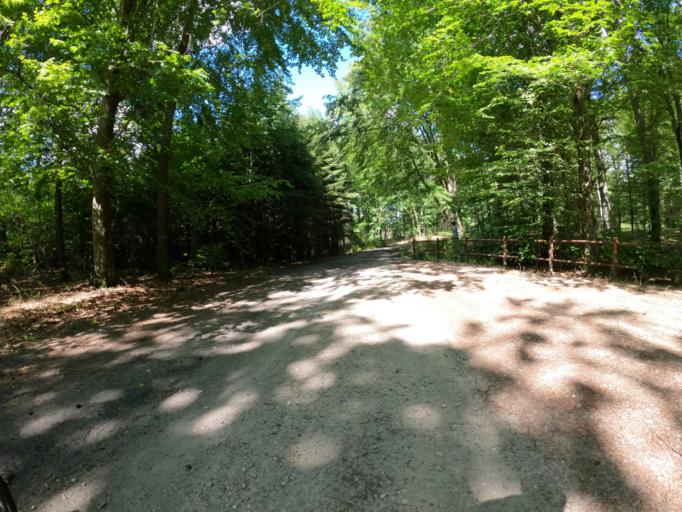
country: PL
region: West Pomeranian Voivodeship
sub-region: Powiat swidwinski
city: Swidwin
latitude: 53.6747
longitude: 15.9008
